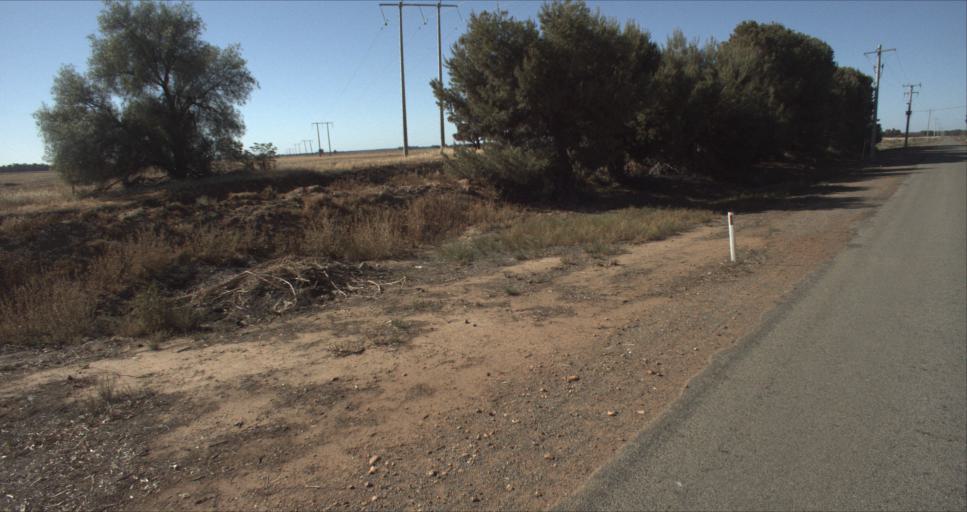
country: AU
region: New South Wales
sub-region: Leeton
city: Leeton
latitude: -34.5745
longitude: 146.3100
